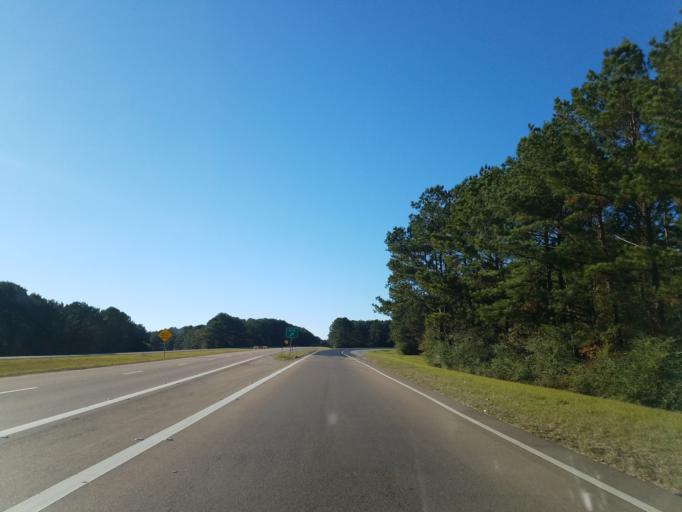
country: US
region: Mississippi
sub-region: Forrest County
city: Hattiesburg
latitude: 31.2387
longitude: -89.3163
